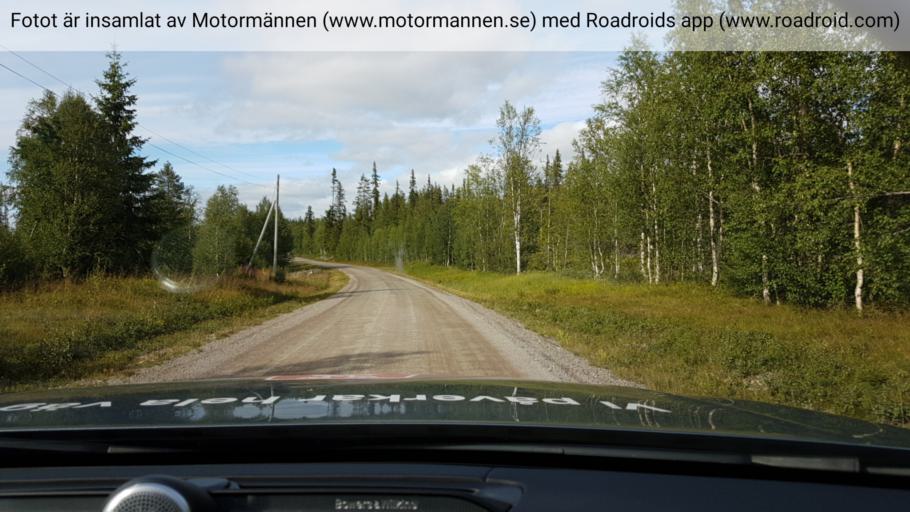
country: SE
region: Jaemtland
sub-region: Stroemsunds Kommun
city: Stroemsund
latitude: 64.5207
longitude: 15.1095
